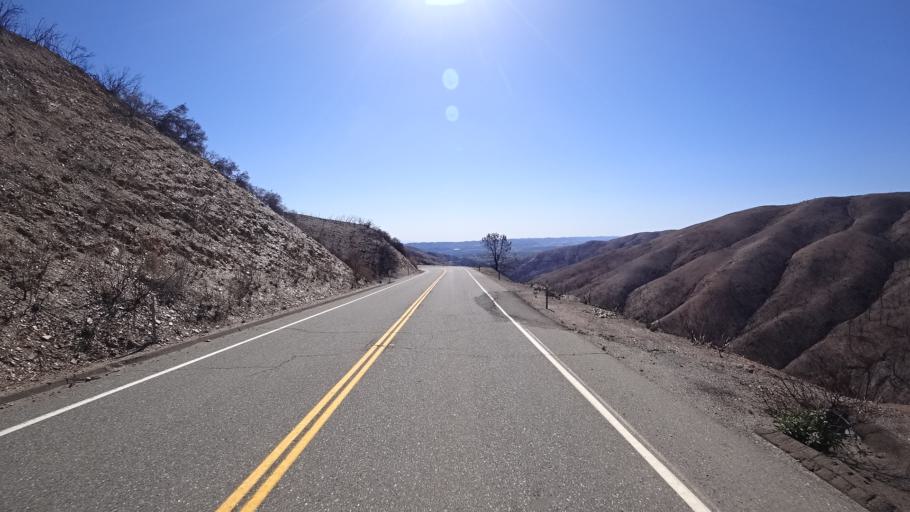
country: US
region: California
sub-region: Tehama County
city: Rancho Tehama Reserve
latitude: 39.6605
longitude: -122.6316
